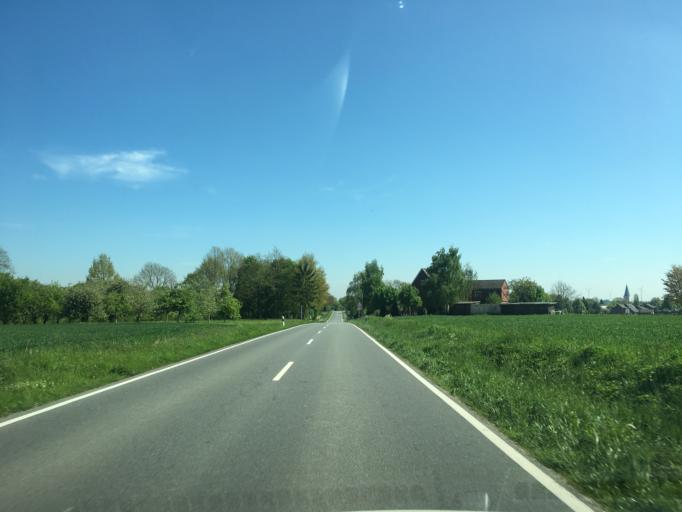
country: DE
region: North Rhine-Westphalia
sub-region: Regierungsbezirk Munster
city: Laer
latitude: 52.0488
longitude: 7.3411
